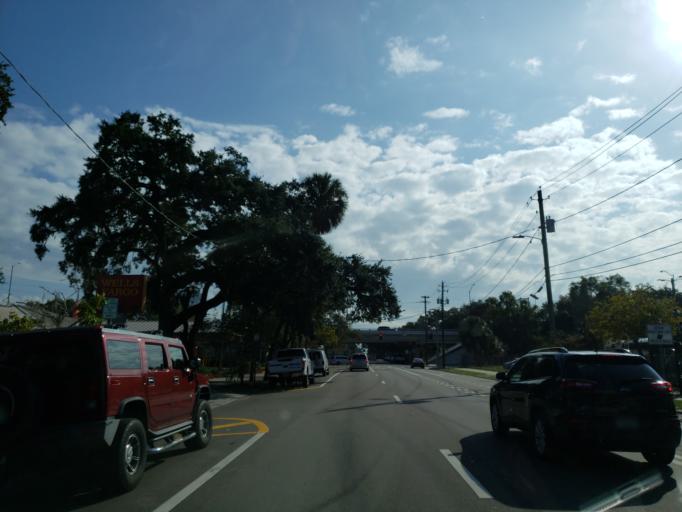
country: US
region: Florida
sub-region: Hillsborough County
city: Tampa
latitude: 27.9440
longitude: -82.4639
